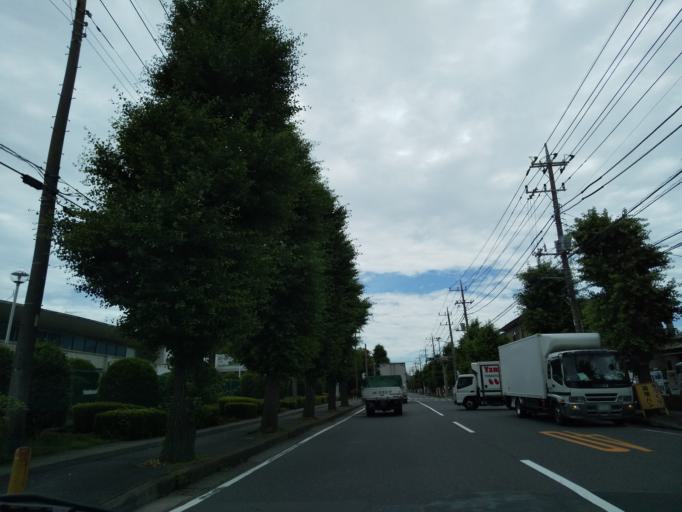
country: JP
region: Kanagawa
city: Zama
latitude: 35.5152
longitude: 139.3563
